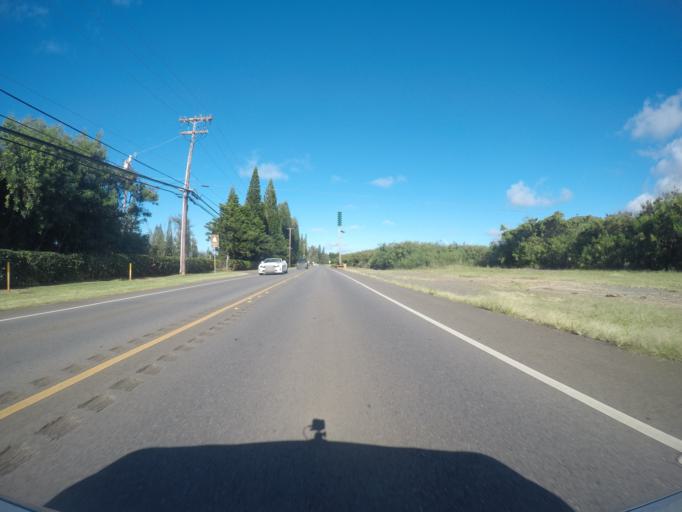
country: US
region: Hawaii
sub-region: Honolulu County
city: Kahuku
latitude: 21.6979
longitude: -157.9873
